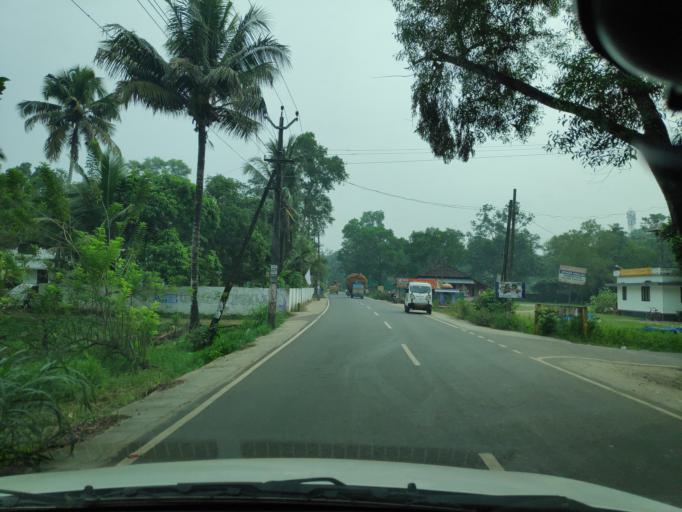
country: IN
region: Kerala
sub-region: Alappuzha
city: Shertallai
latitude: 9.6083
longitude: 76.3403
